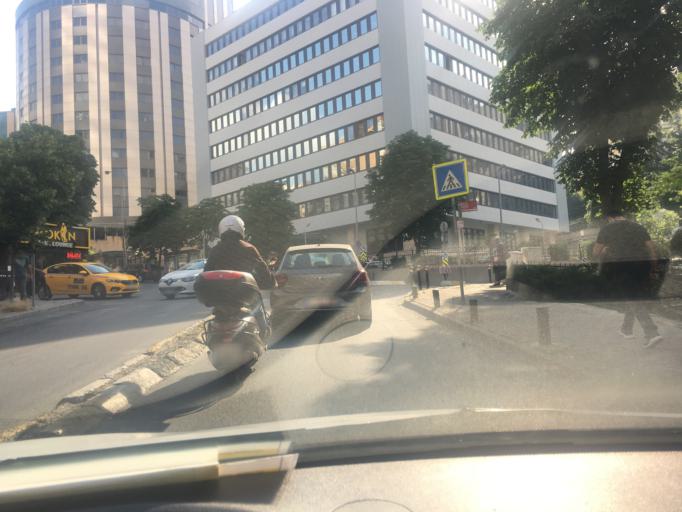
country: TR
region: Istanbul
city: Sisli
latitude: 41.0643
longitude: 29.0022
